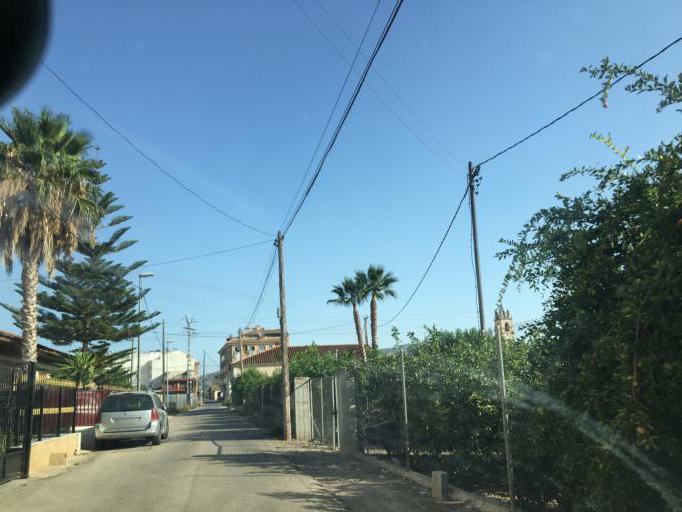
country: ES
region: Murcia
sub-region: Murcia
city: Santomera
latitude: 38.0207
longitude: -1.0498
